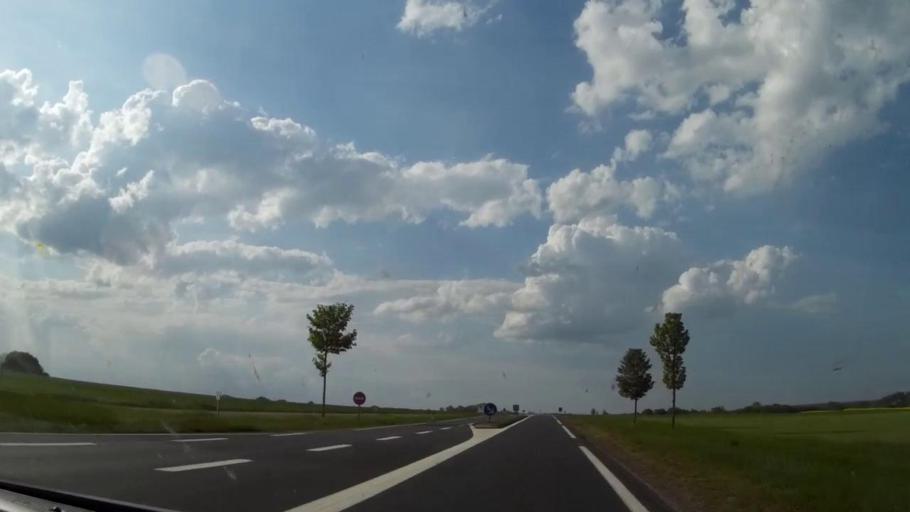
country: FR
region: Centre
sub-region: Departement du Loir-et-Cher
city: Aze
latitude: 47.8846
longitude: 0.9497
